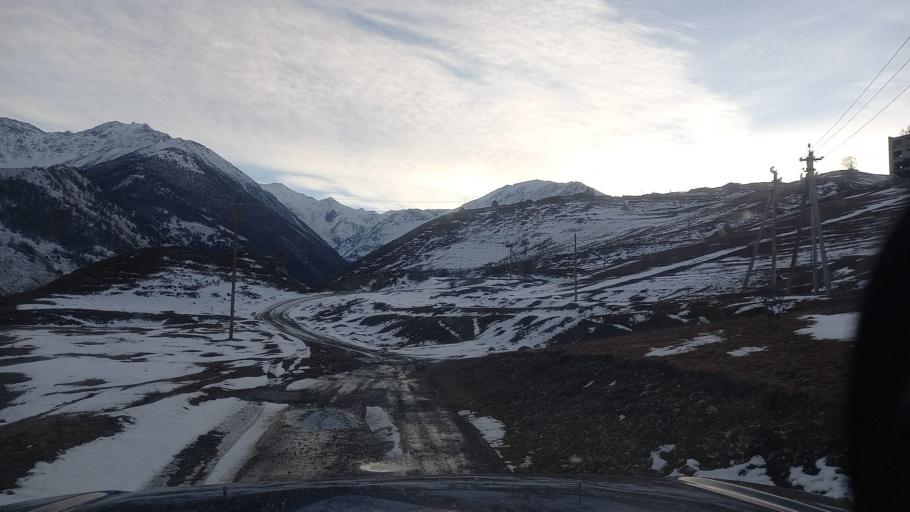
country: RU
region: Ingushetiya
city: Dzhayrakh
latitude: 42.8451
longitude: 44.5135
